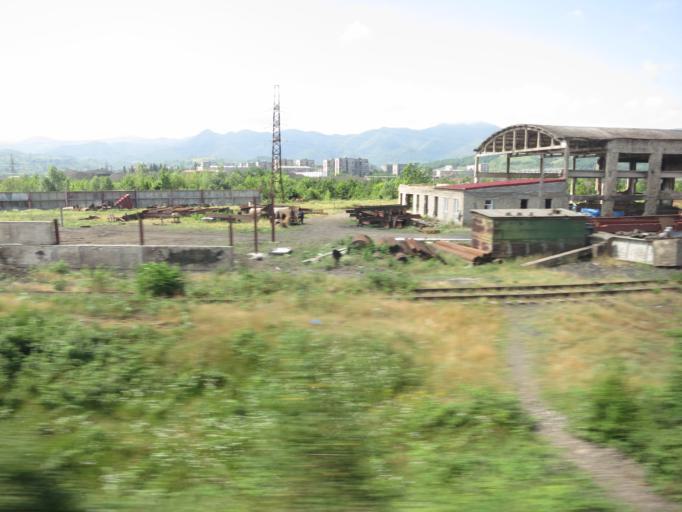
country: GE
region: Imereti
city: Zestap'oni
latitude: 42.1166
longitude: 43.0178
